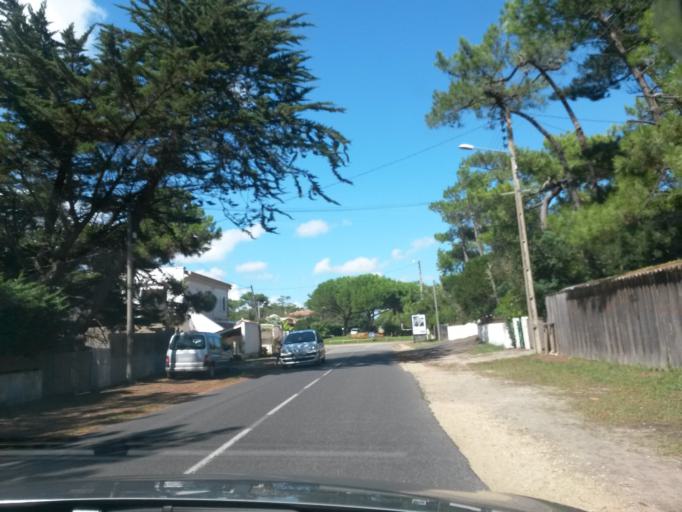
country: FR
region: Aquitaine
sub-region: Departement de la Gironde
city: Arcachon
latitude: 44.6542
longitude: -1.2489
